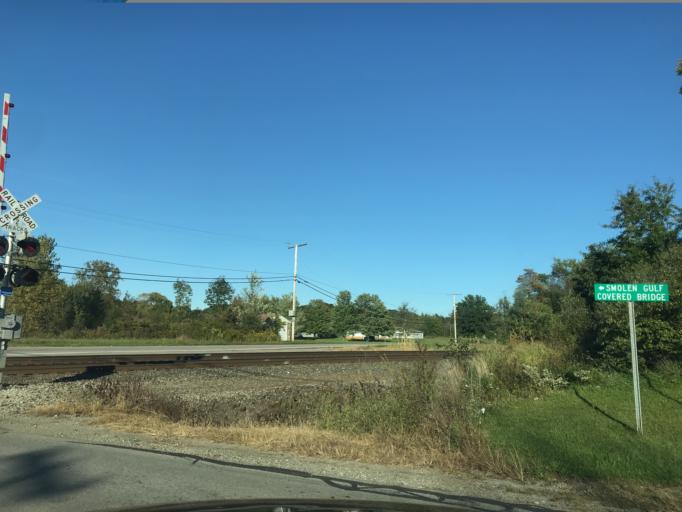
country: US
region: Ohio
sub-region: Ashtabula County
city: Edgewood
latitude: 41.8440
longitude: -80.7560
